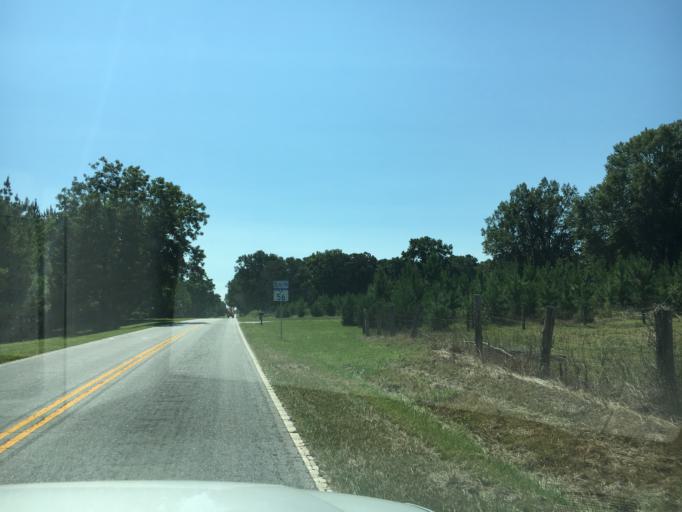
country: US
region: South Carolina
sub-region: Laurens County
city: Joanna
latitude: 34.4103
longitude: -81.8620
